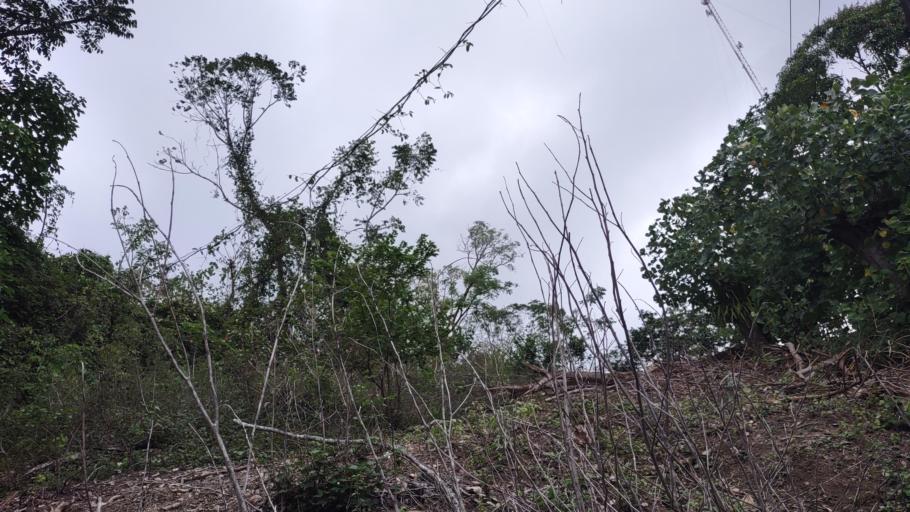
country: MX
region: Veracruz
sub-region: Coatzintla
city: Manuel Maria Contreras
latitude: 20.4114
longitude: -97.4561
